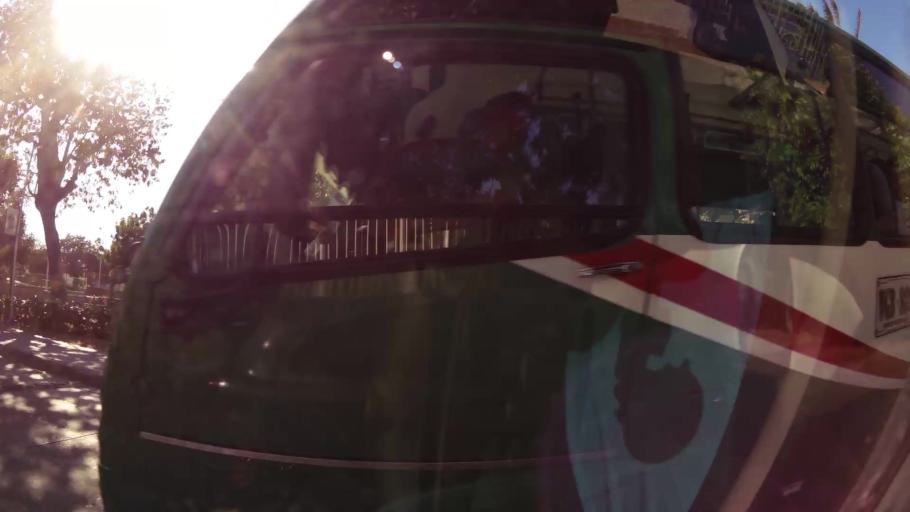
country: CO
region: Atlantico
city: Barranquilla
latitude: 10.9709
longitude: -74.7835
